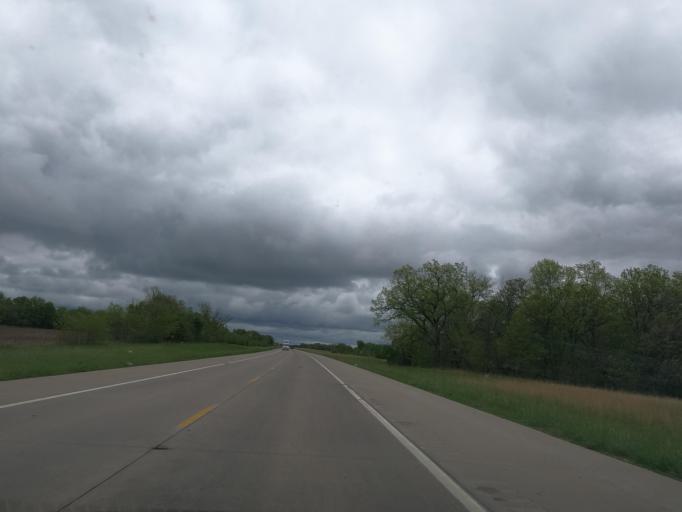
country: US
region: Kansas
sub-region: Labette County
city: Parsons
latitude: 37.3452
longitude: -95.3464
